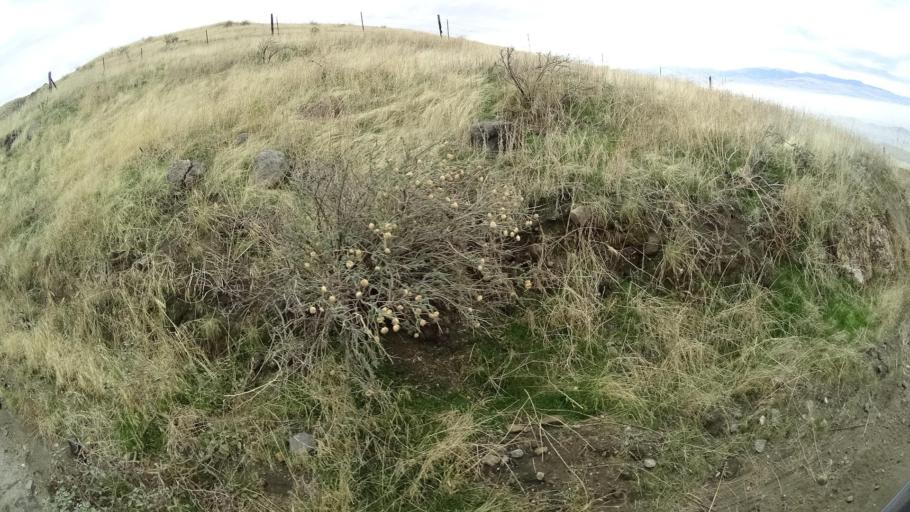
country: US
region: California
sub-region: Kern County
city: Arvin
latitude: 35.1359
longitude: -118.7794
